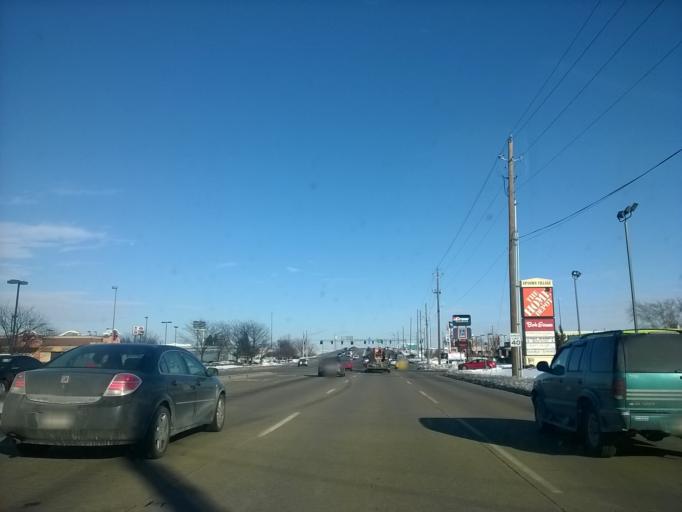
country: US
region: Indiana
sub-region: Hamilton County
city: Fishers
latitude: 39.9270
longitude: -86.0359
